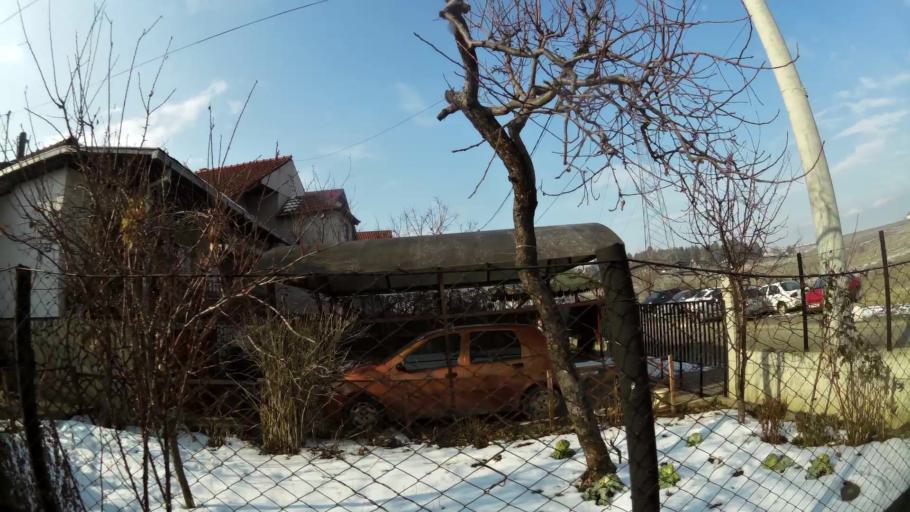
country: MK
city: Creshevo
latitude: 42.0129
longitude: 21.4951
